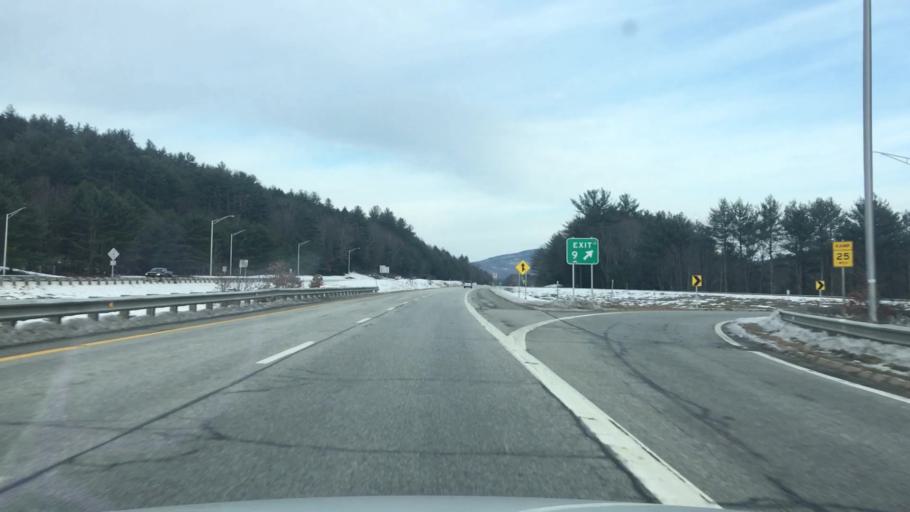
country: US
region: New Hampshire
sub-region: Merrimack County
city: Henniker
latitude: 43.2899
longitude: -71.8366
